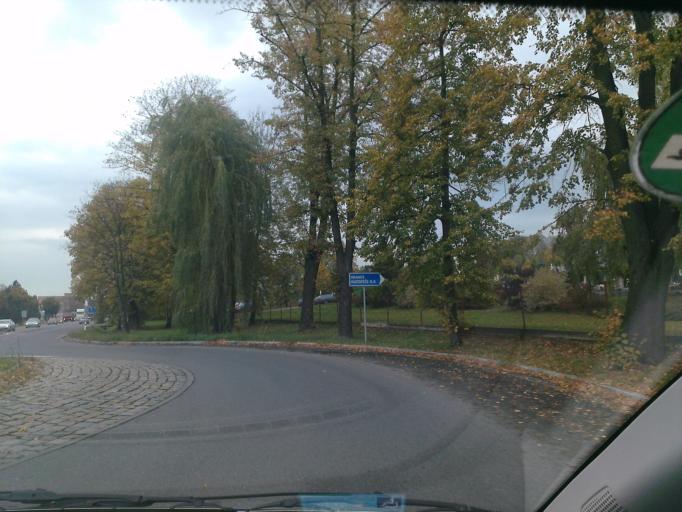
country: CZ
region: Zlin
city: Valasske Mezirici
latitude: 49.4849
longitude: 17.9649
